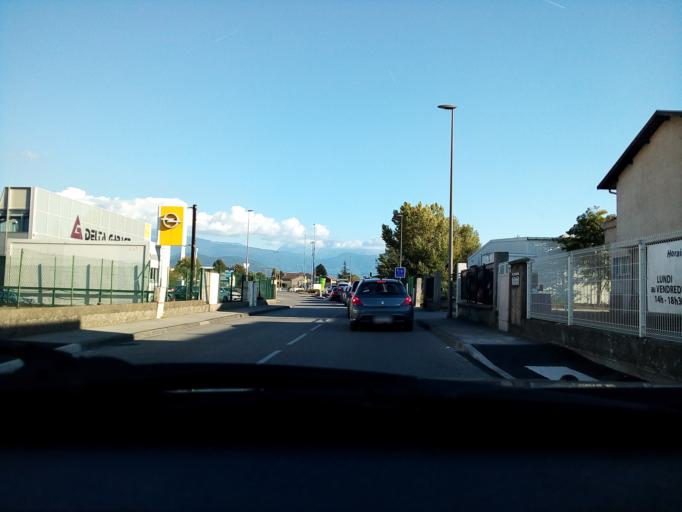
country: FR
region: Rhone-Alpes
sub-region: Departement de l'Isere
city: Fontaine
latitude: 45.2063
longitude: 5.6814
